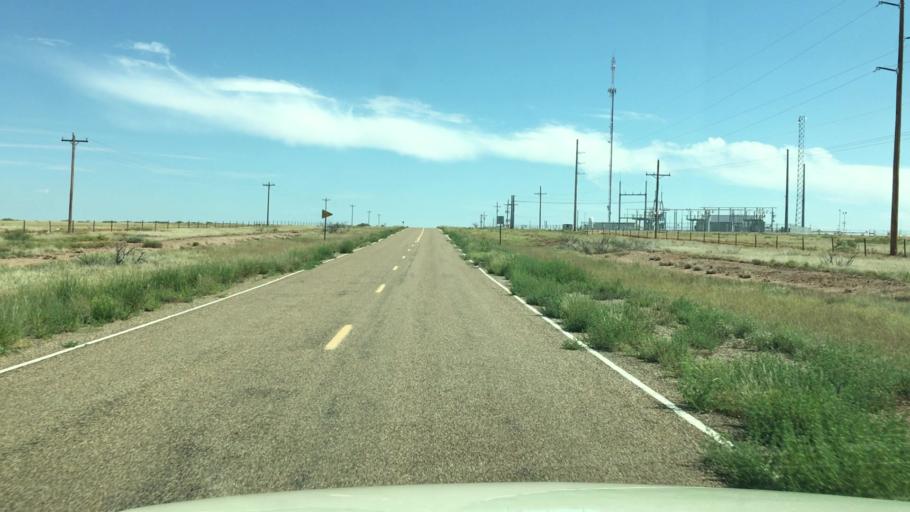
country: US
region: New Mexico
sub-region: Chaves County
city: Roswell
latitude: 33.9616
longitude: -104.5834
